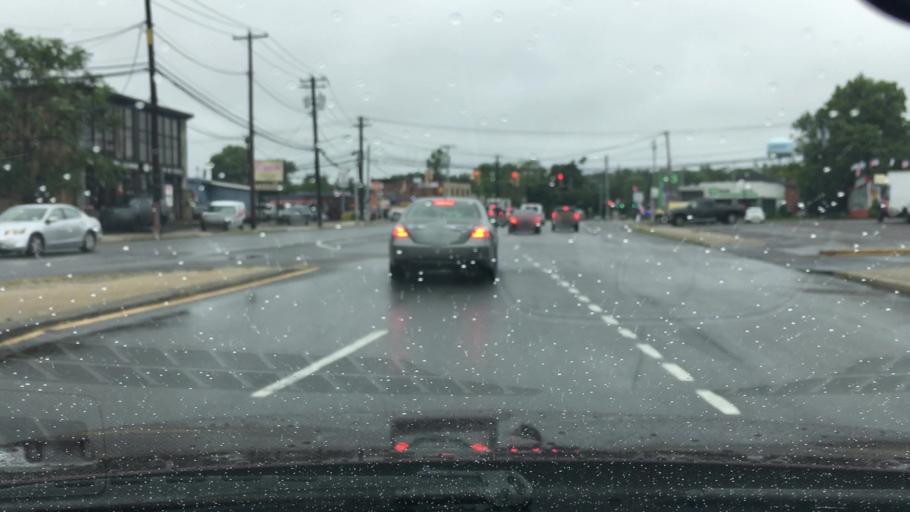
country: US
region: New York
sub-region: Nassau County
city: Plainview
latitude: 40.7754
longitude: -73.4664
